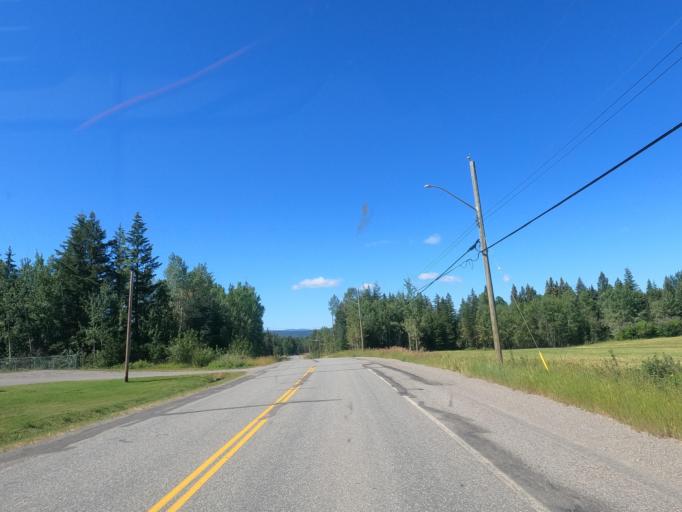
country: CA
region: British Columbia
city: Quesnel
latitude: 53.0210
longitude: -122.4551
